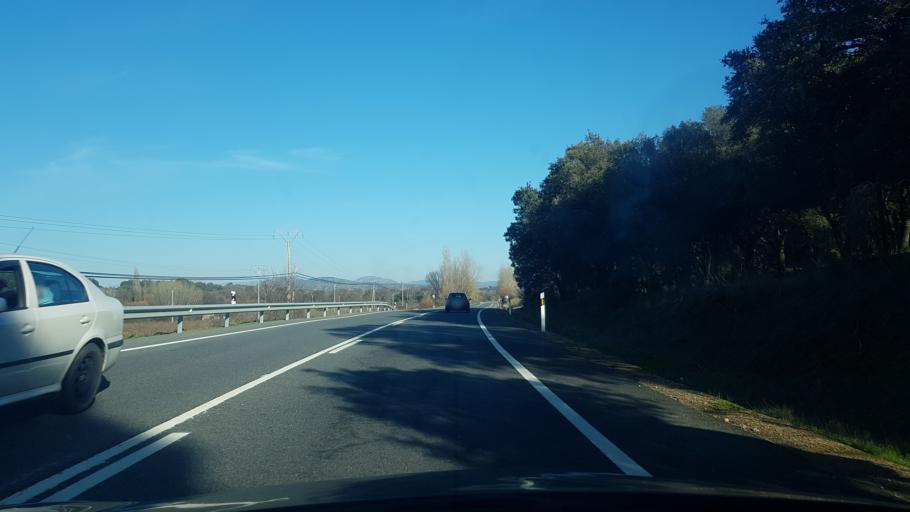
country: ES
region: Madrid
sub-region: Provincia de Madrid
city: Rozas de Puerto Real
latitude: 40.3407
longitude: -4.4594
